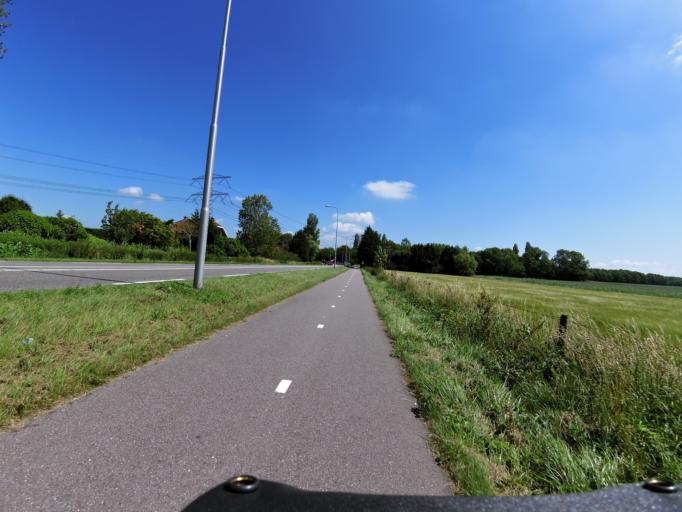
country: NL
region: South Holland
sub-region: Gemeente Brielle
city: Brielle
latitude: 51.9110
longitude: 4.1240
